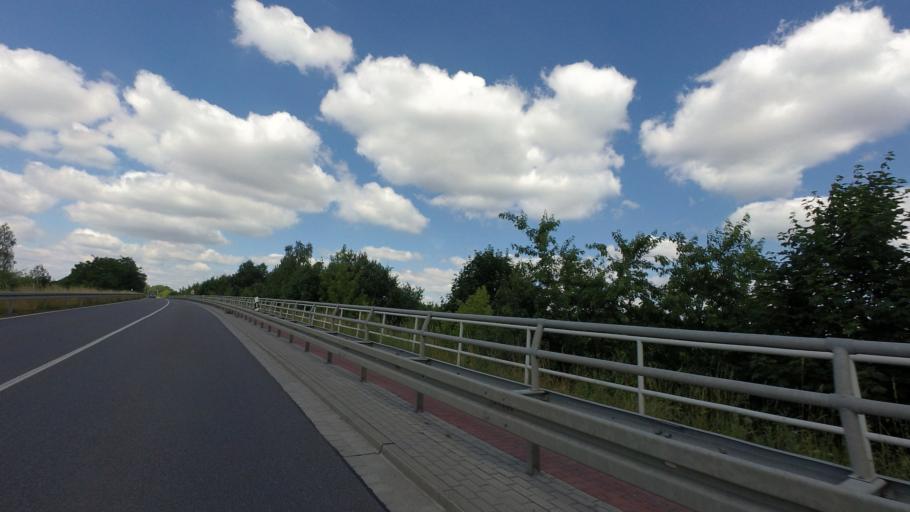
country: DE
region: Brandenburg
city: Grossraschen
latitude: 51.5833
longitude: 14.0205
